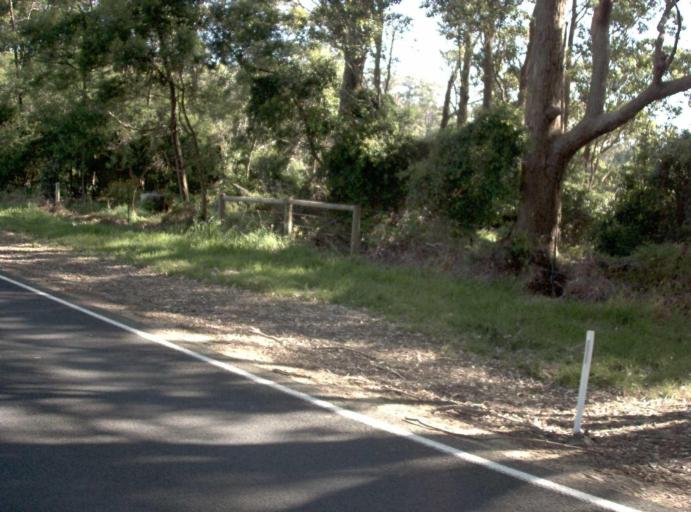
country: AU
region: Victoria
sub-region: East Gippsland
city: Lakes Entrance
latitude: -37.7497
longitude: 148.5185
